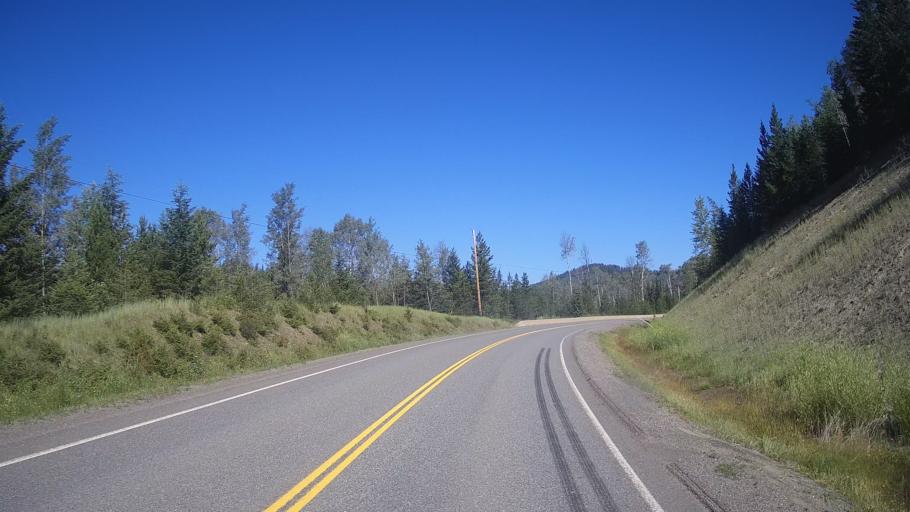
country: CA
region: British Columbia
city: Kamloops
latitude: 51.4779
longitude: -120.5613
